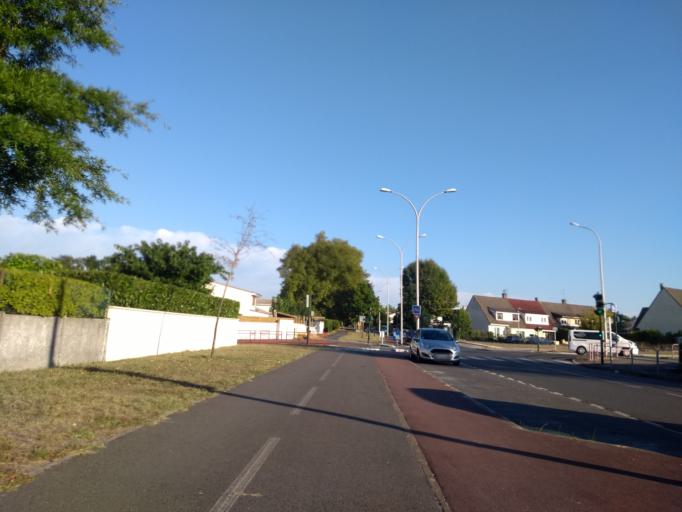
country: FR
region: Aquitaine
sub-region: Departement de la Gironde
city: Pessac
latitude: 44.8041
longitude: -0.6679
